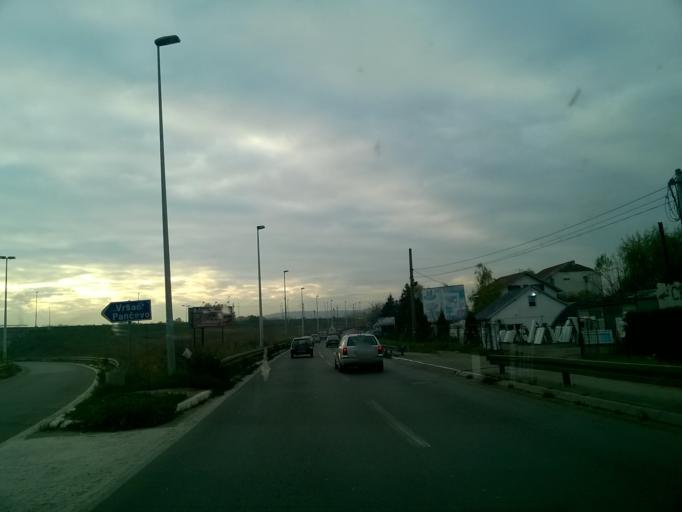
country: RS
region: Central Serbia
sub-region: Belgrade
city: Palilula
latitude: 44.8383
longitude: 20.4924
